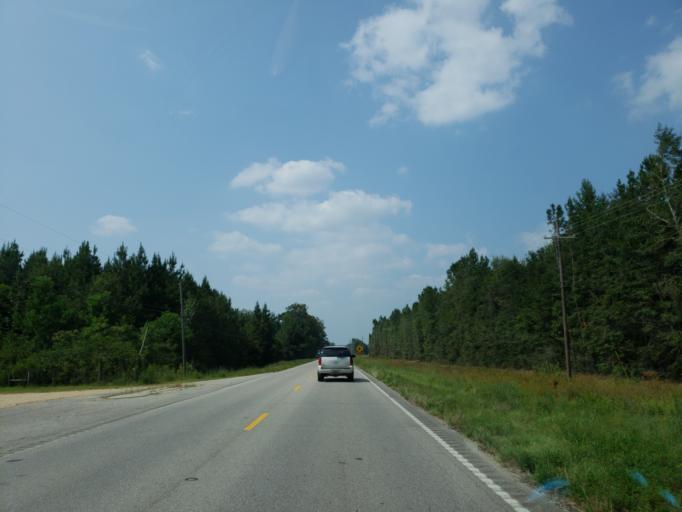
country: US
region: Mississippi
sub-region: Forrest County
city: Glendale
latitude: 31.4299
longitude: -89.2826
